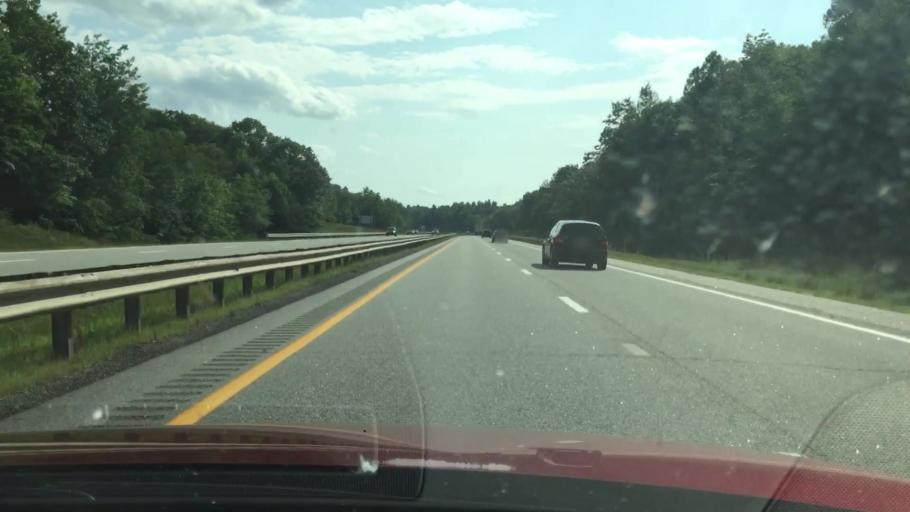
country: US
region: Maine
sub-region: Cumberland County
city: New Gloucester
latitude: 44.0118
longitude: -70.3005
